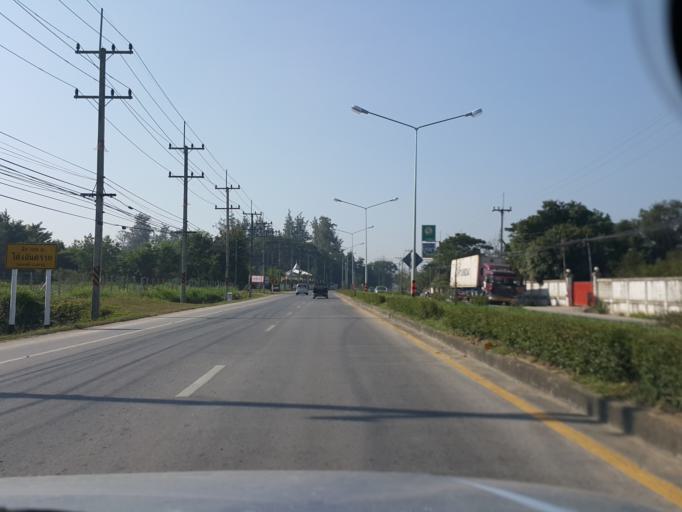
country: TH
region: Chiang Mai
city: San Pa Tong
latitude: 18.5735
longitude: 98.8796
